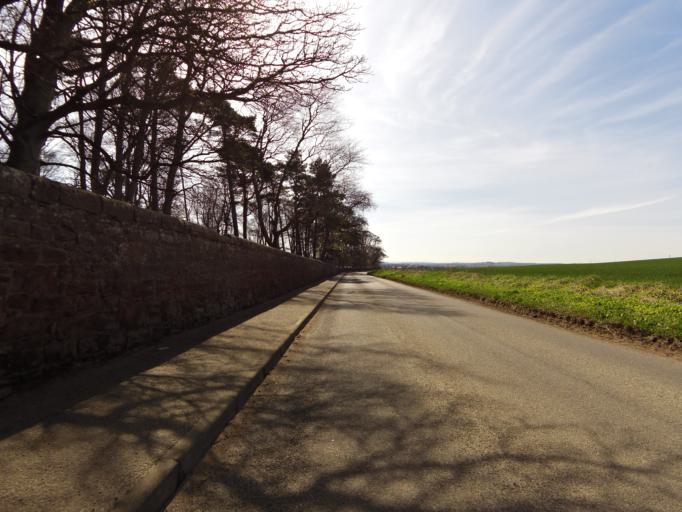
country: GB
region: Scotland
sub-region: Angus
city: Arbroath
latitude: 56.5774
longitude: -2.5620
